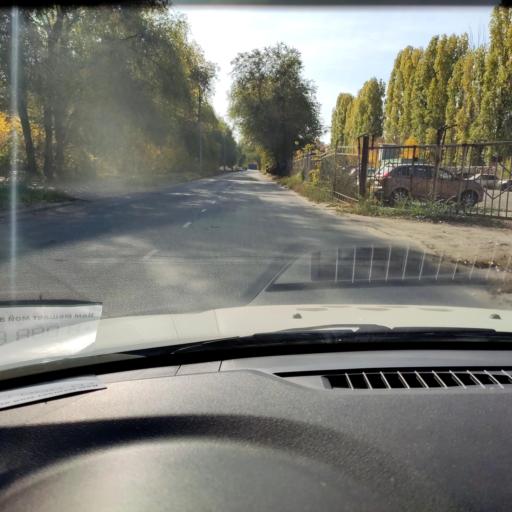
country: RU
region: Samara
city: Tol'yatti
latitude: 53.5540
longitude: 49.3090
